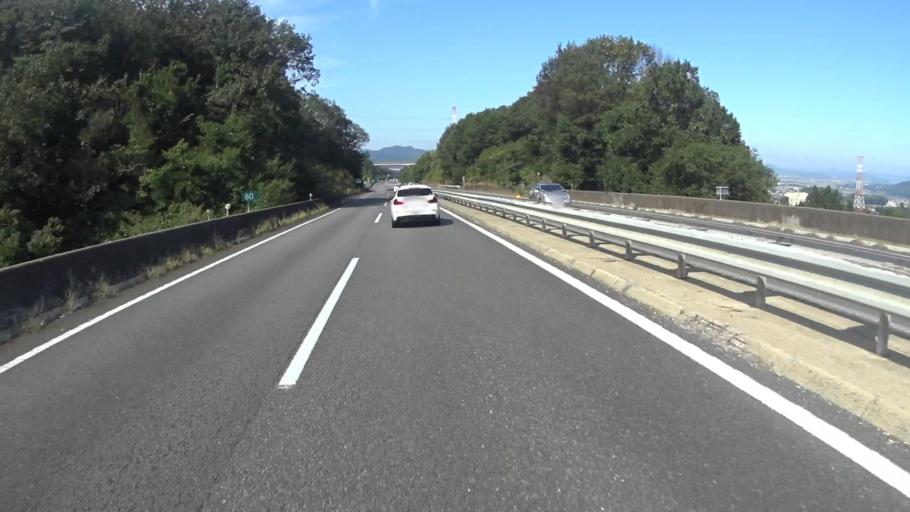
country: JP
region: Kyoto
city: Kameoka
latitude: 34.9899
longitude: 135.6266
